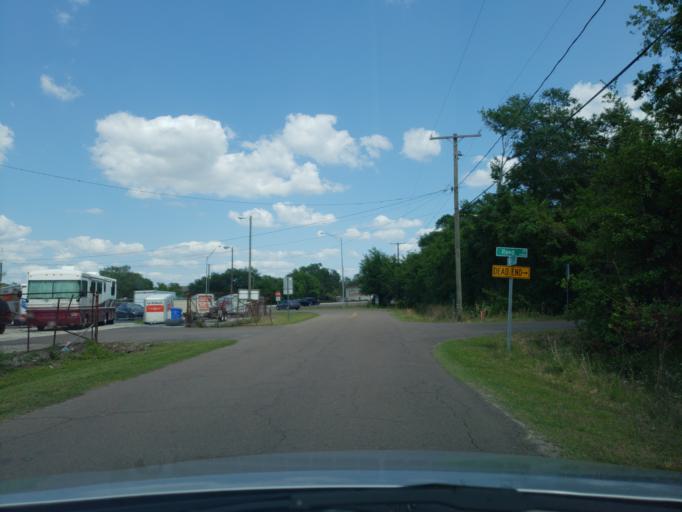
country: US
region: Florida
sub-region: Hillsborough County
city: Riverview
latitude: 27.8882
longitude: -82.3335
